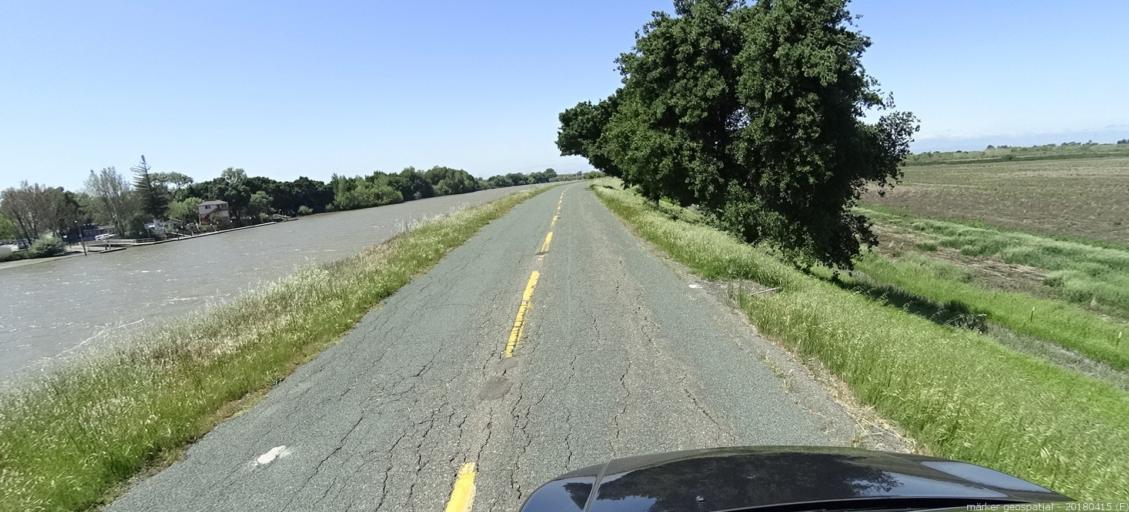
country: US
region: California
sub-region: Solano County
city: Rio Vista
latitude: 38.1735
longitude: -121.6406
